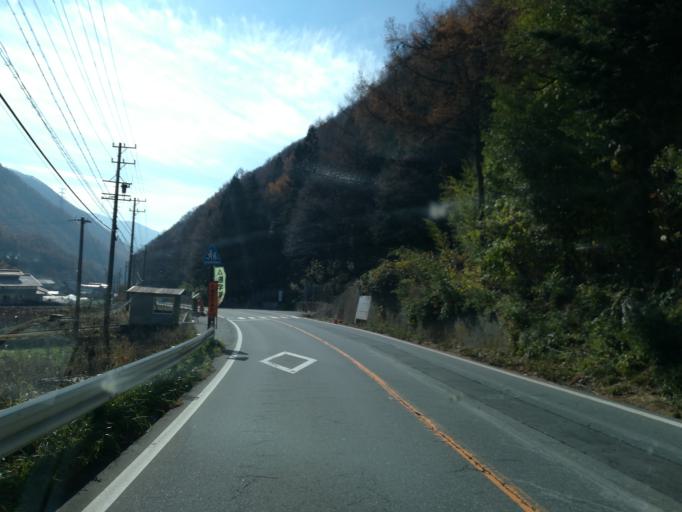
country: JP
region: Nagano
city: Ueda
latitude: 36.4771
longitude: 138.3456
